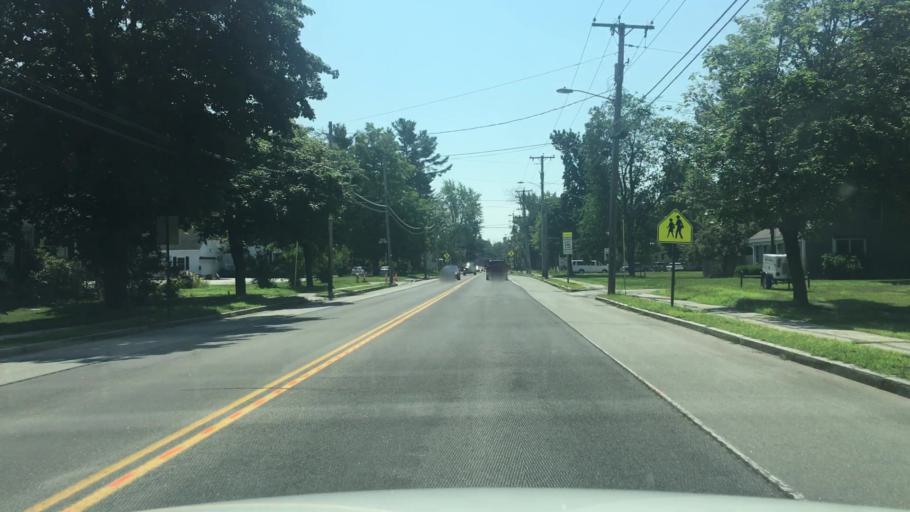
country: US
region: Maine
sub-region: Cumberland County
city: New Gloucester
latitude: 43.8893
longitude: -70.3340
